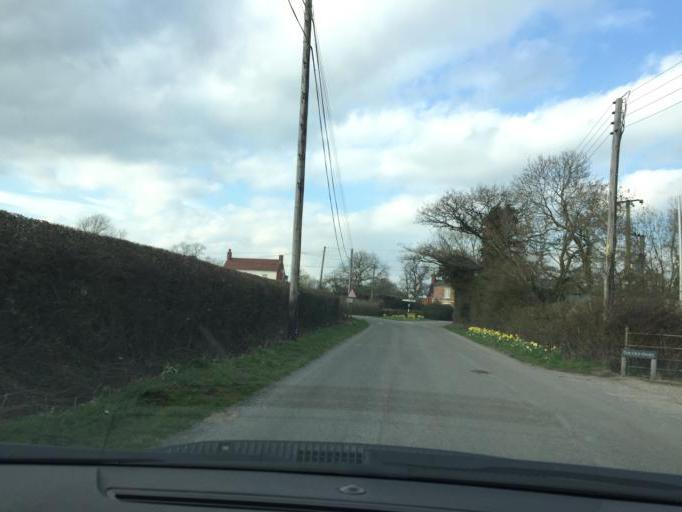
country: GB
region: England
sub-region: Coventry
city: Keresley
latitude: 52.4418
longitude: -1.5725
